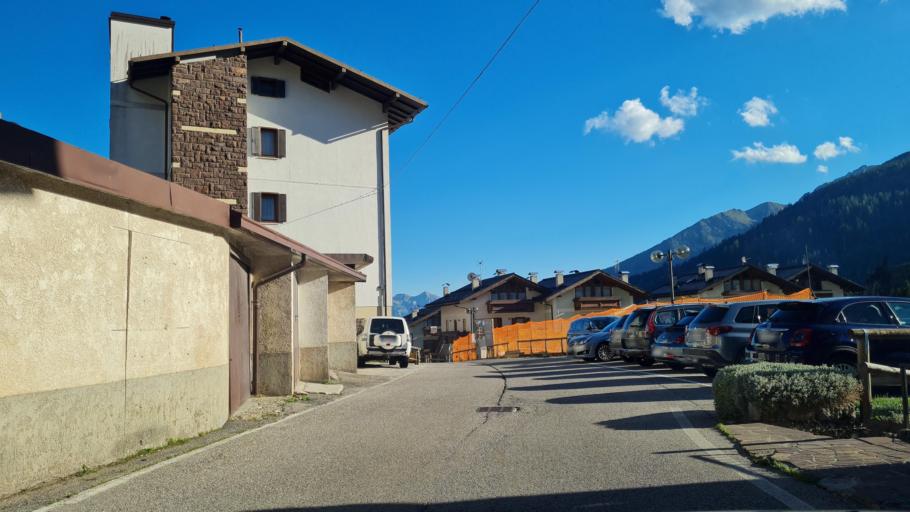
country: IT
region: Trentino-Alto Adige
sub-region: Provincia di Trento
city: Siror
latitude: 46.2606
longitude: 11.8044
